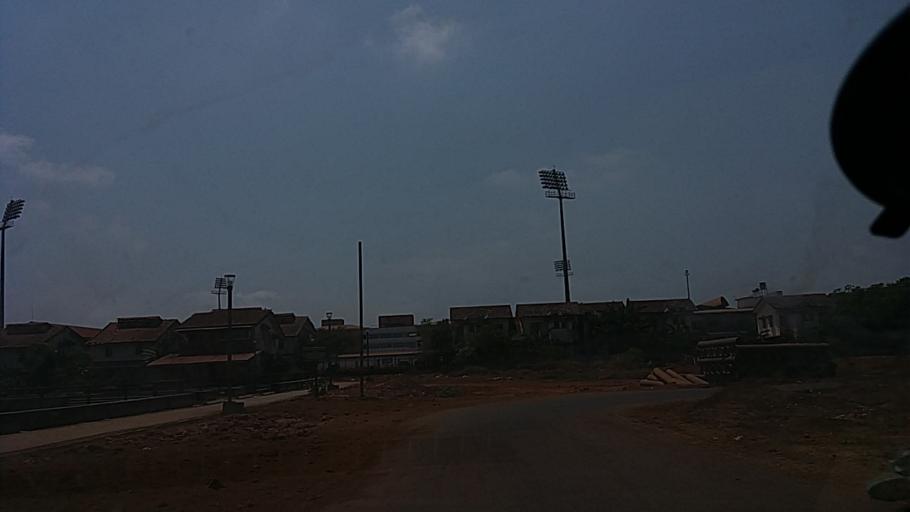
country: IN
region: Goa
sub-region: North Goa
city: Serula
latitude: 15.5247
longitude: 73.8316
